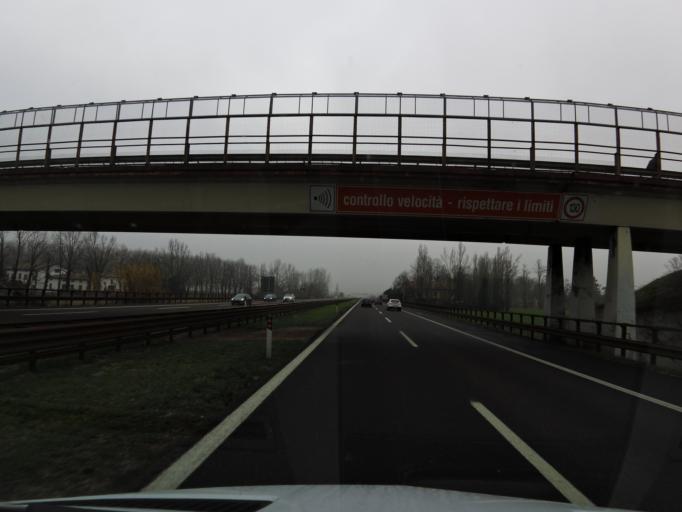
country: IT
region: Emilia-Romagna
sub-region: Provincia di Modena
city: Santa Croce Scuole
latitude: 44.7759
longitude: 10.8465
